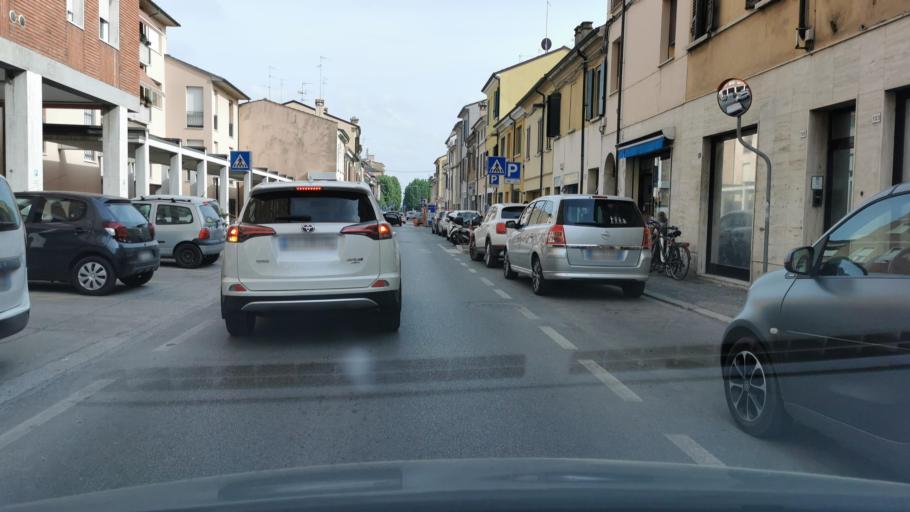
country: IT
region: Emilia-Romagna
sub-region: Provincia di Ravenna
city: Ravenna
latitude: 44.4106
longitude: 12.2070
